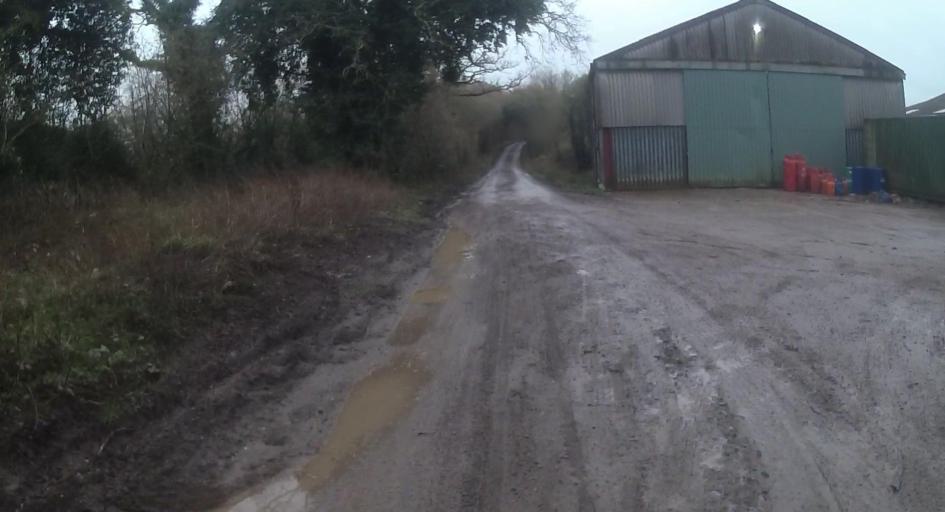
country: GB
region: England
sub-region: Hampshire
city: Kings Worthy
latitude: 51.1115
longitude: -1.2526
